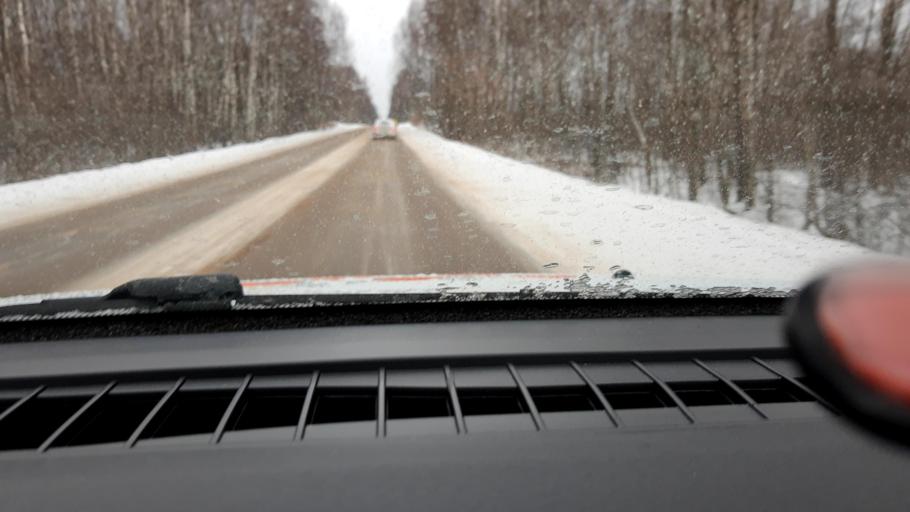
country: RU
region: Nizjnij Novgorod
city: Kstovo
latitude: 56.2991
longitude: 44.2659
